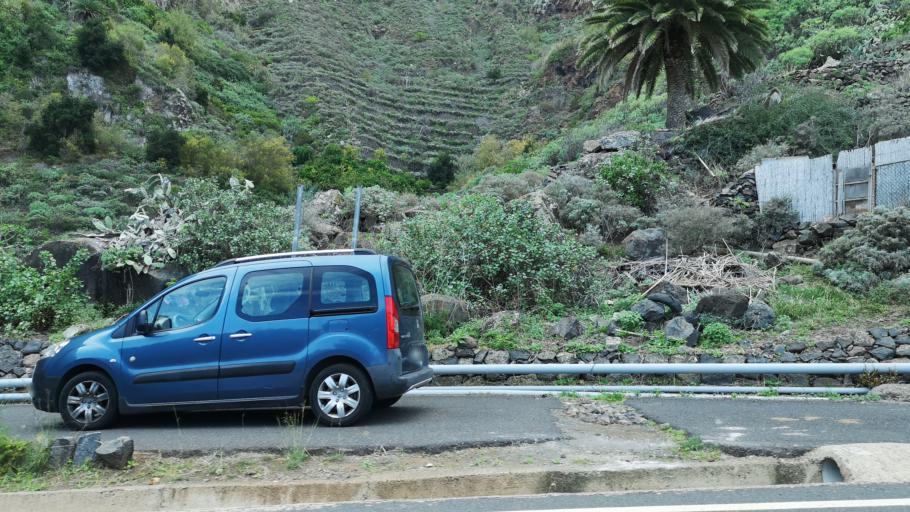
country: ES
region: Canary Islands
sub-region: Provincia de Santa Cruz de Tenerife
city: Agulo
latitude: 28.1852
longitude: -17.1962
